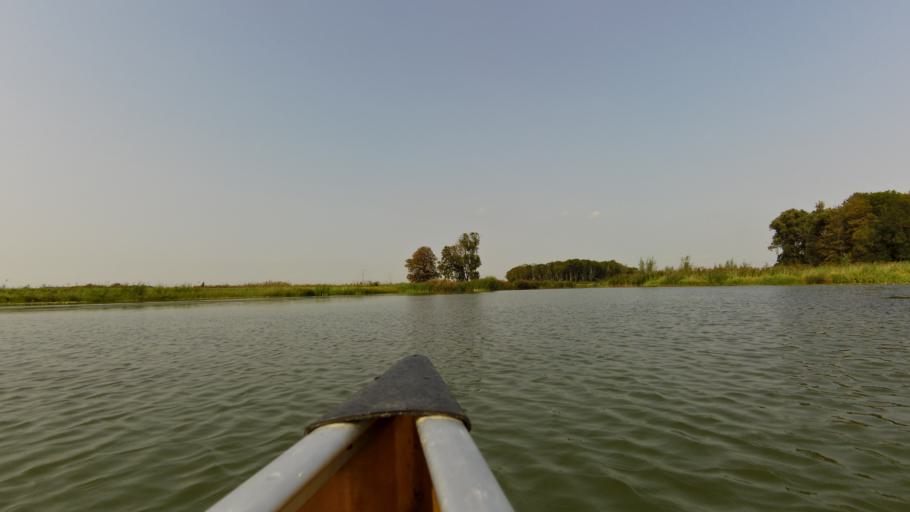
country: NL
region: South Holland
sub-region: Gemeente Sliedrecht
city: Sliedrecht
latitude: 51.7711
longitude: 4.8204
